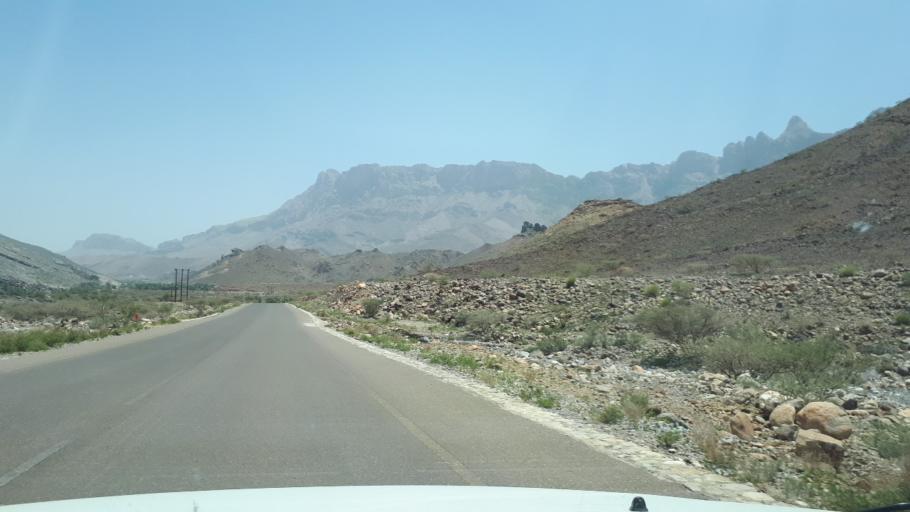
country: OM
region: Muhafazat ad Dakhiliyah
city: Bahla'
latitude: 23.1802
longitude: 57.1424
